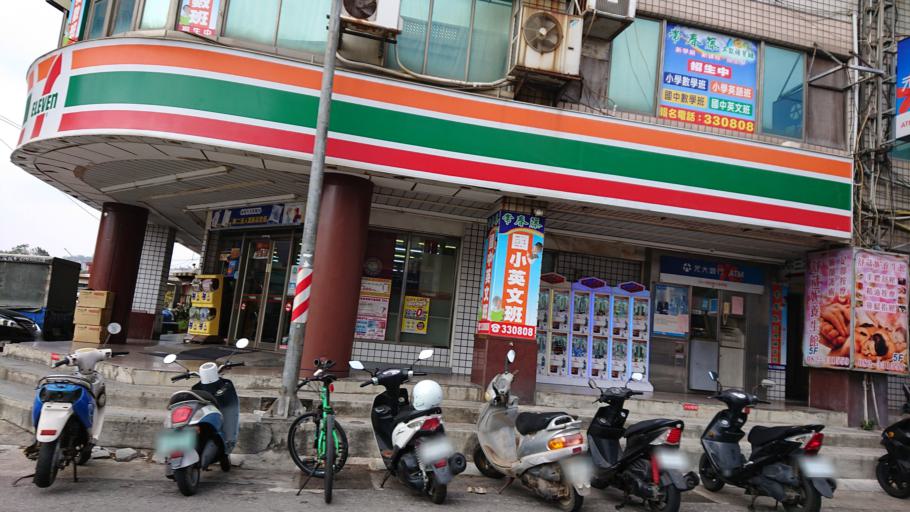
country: TW
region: Fukien
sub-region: Kinmen
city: Jincheng
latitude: 24.4425
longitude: 118.4143
